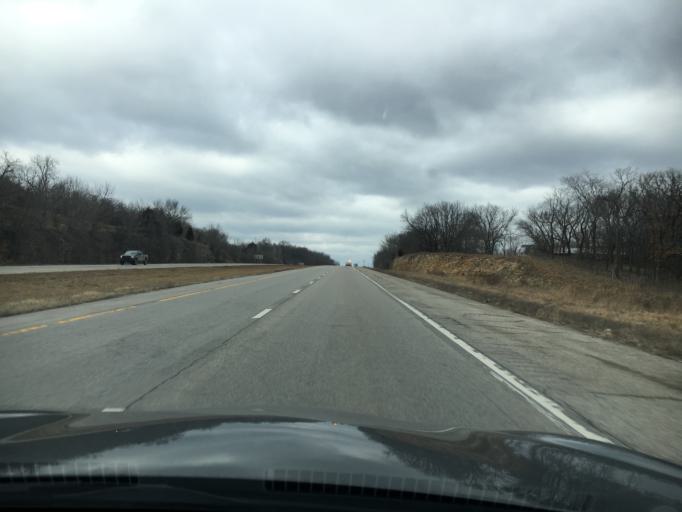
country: US
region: Missouri
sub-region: Cass County
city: Belton
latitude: 38.8144
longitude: -94.6757
